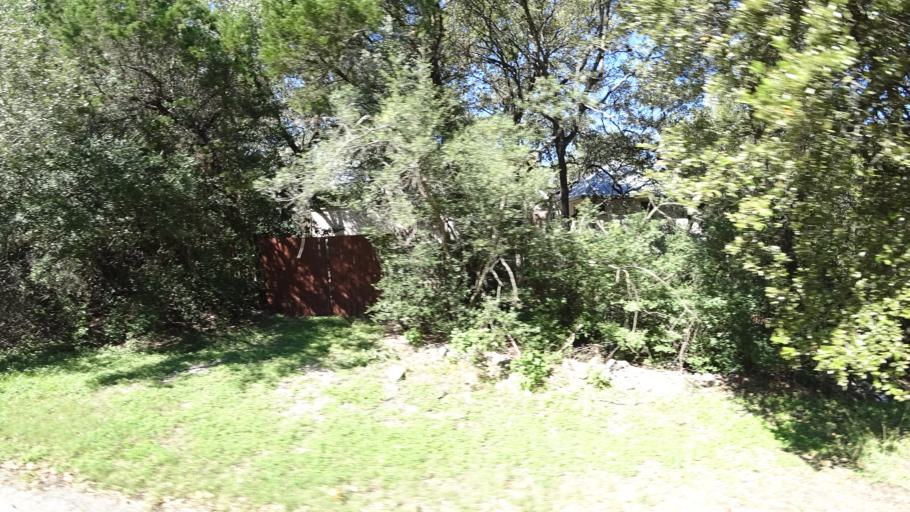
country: US
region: Texas
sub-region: Travis County
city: West Lake Hills
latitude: 30.3122
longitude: -97.7825
